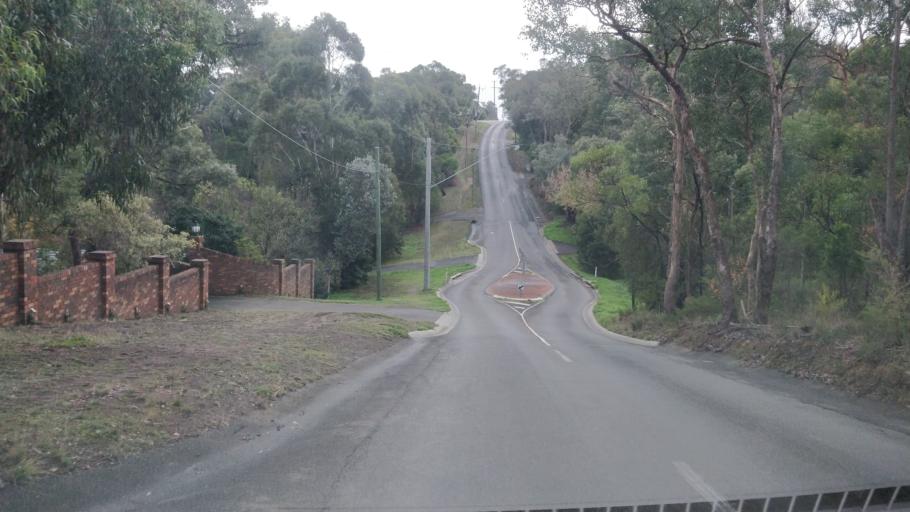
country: AU
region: Victoria
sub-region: Nillumbik
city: Research
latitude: -37.7125
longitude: 145.1746
